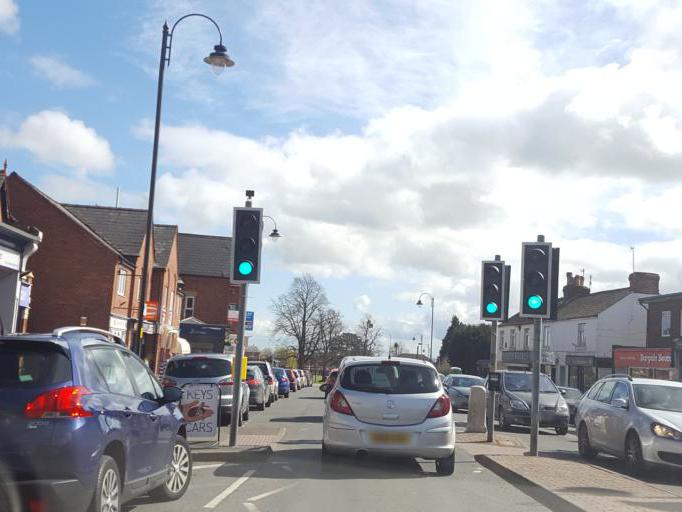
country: GB
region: England
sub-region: Worcestershire
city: Great Malvern
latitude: 52.1086
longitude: -2.3114
